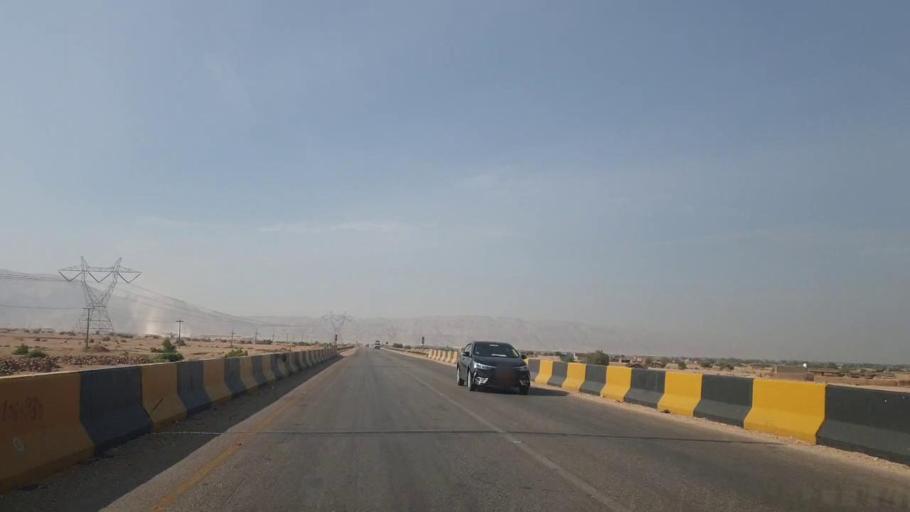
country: PK
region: Sindh
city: Sehwan
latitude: 26.2059
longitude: 67.9305
